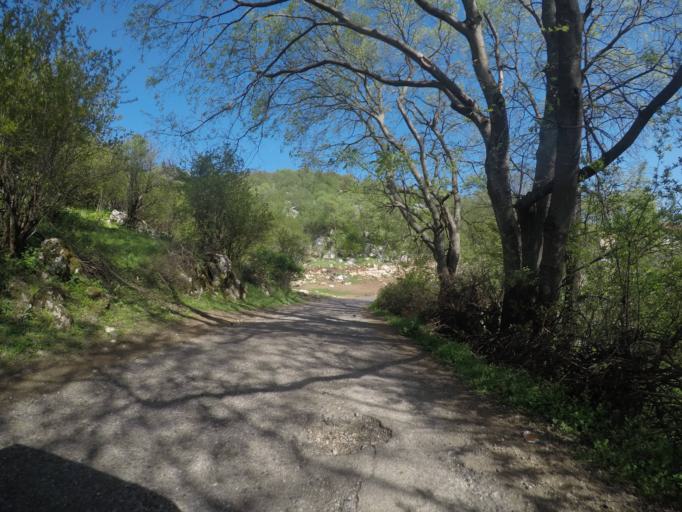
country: ME
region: Danilovgrad
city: Danilovgrad
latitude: 42.5341
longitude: 19.0890
